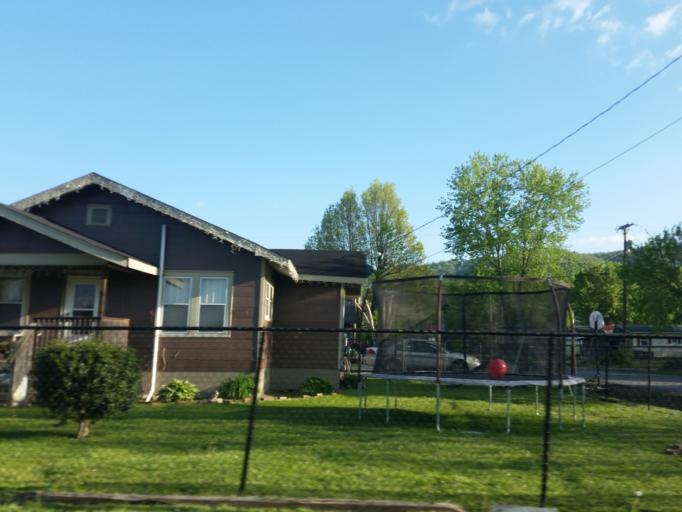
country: US
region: Kentucky
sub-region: Bell County
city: Middlesboro
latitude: 36.6027
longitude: -83.7278
